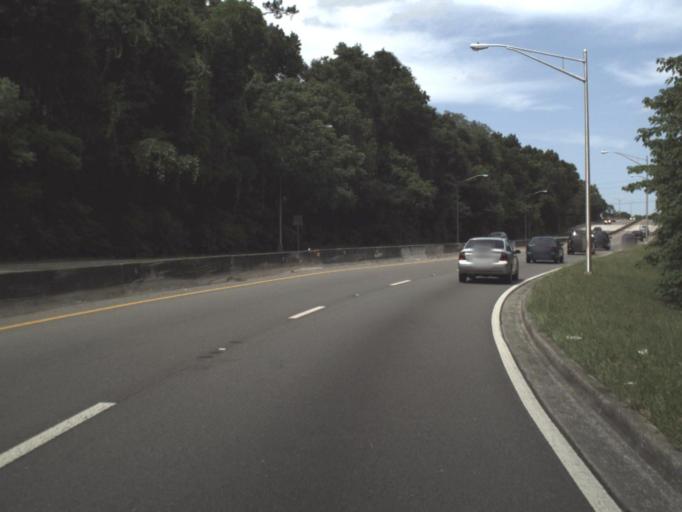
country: US
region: Florida
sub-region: Duval County
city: Jacksonville
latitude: 30.2926
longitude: -81.7239
